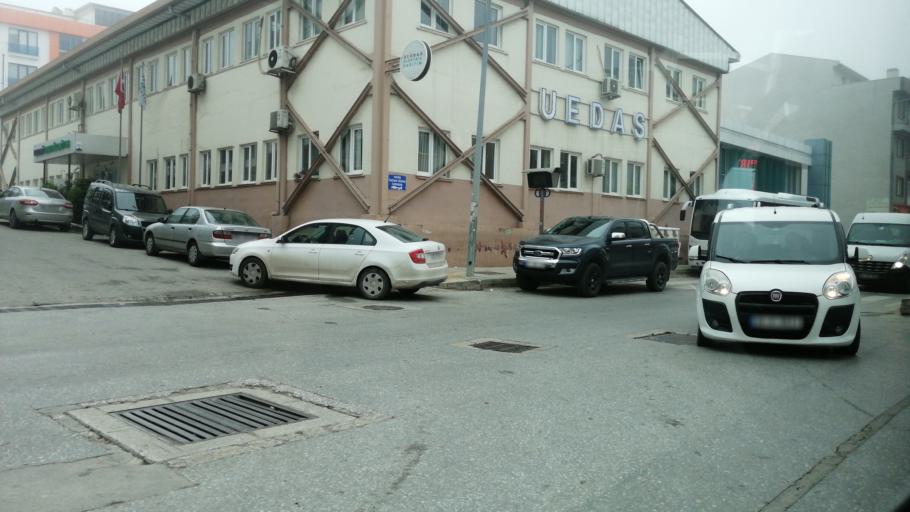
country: TR
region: Yalova
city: Yalova
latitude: 40.6534
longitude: 29.2738
